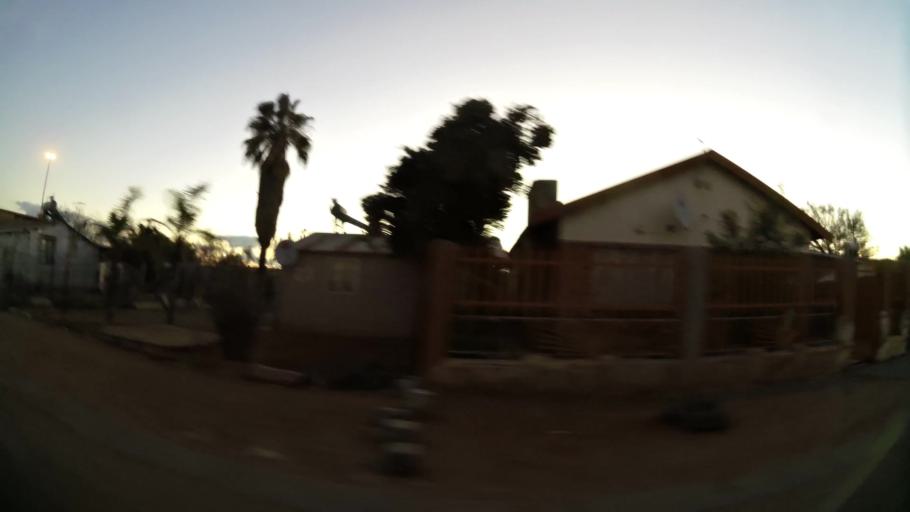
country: ZA
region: Northern Cape
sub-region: Frances Baard District Municipality
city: Kimberley
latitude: -28.7133
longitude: 24.7629
